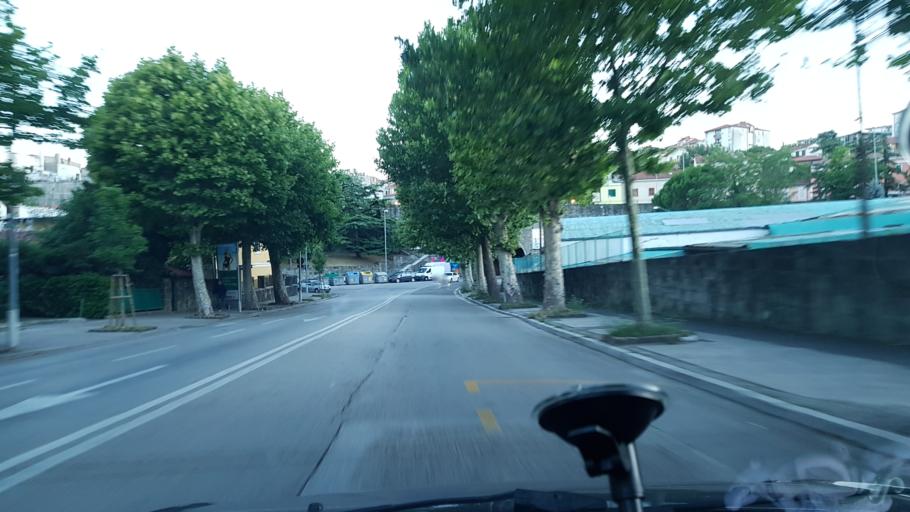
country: IT
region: Friuli Venezia Giulia
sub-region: Provincia di Trieste
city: Trieste
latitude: 45.6316
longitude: 13.7915
